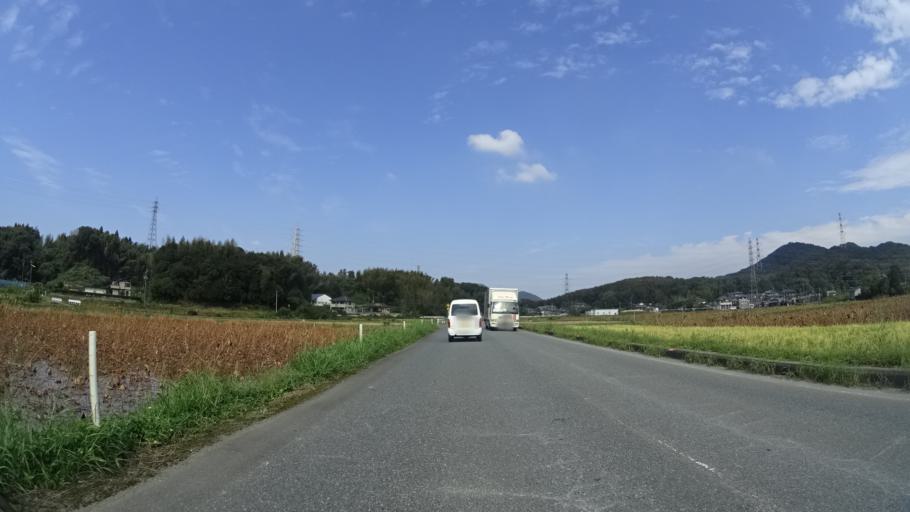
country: JP
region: Kumamoto
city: Matsubase
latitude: 32.6536
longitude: 130.7160
